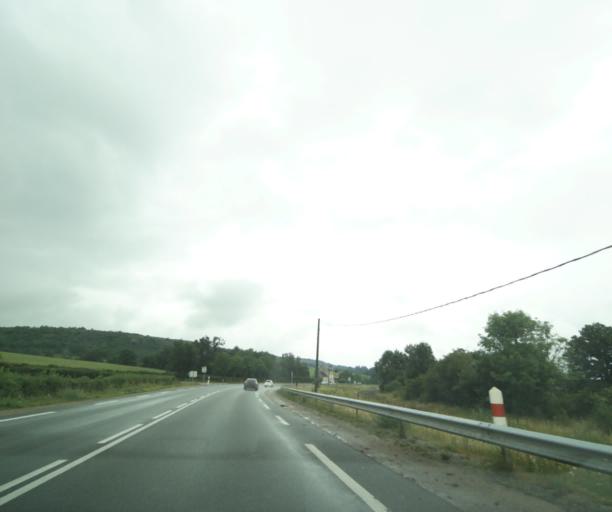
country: FR
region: Midi-Pyrenees
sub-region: Departement de l'Aveyron
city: La Loubiere
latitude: 44.3906
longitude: 2.6757
